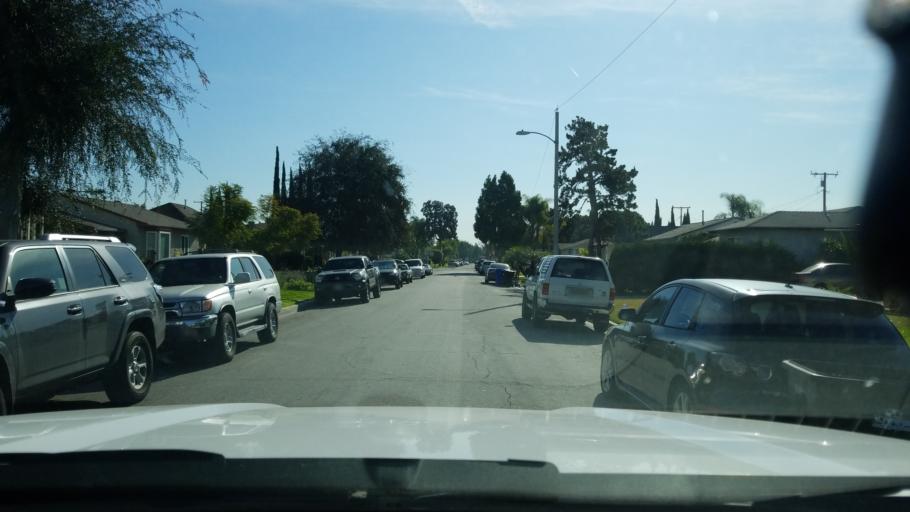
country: US
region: California
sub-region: Los Angeles County
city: West Whittier-Los Nietos
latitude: 33.9801
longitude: -118.0697
